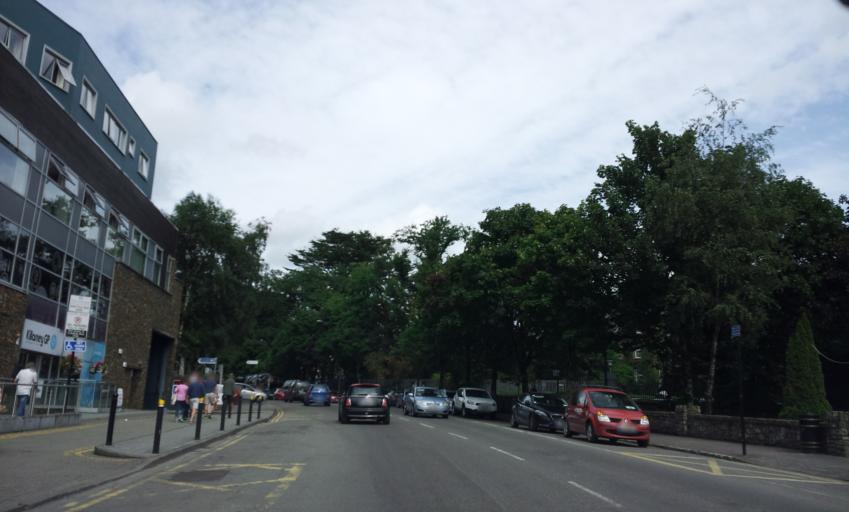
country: IE
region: Munster
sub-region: Ciarrai
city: Cill Airne
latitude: 52.0582
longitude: -9.5056
